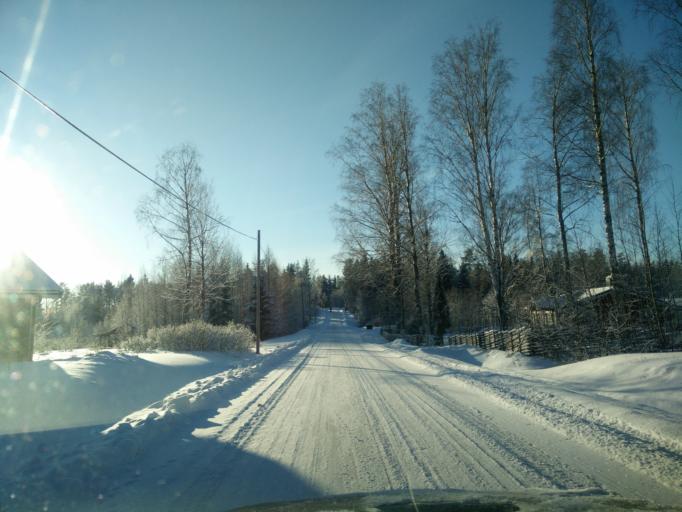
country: SE
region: Vaesternorrland
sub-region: Sundsvalls Kommun
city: Njurundabommen
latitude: 62.2296
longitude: 17.5018
